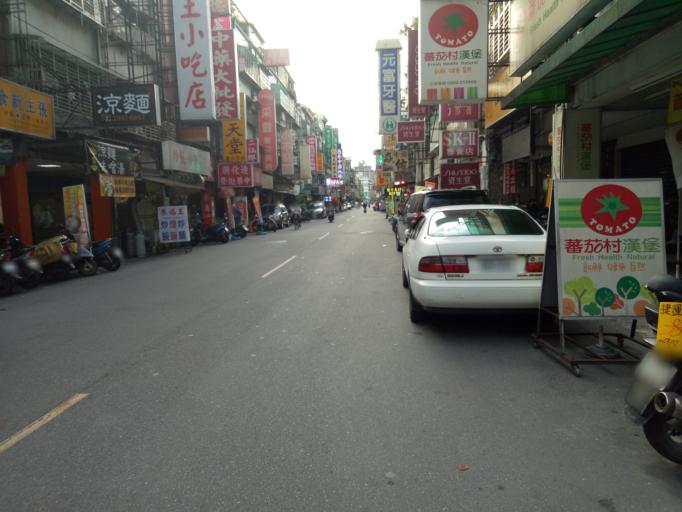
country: TW
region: Taipei
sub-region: Taipei
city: Banqiao
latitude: 25.0456
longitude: 121.4514
